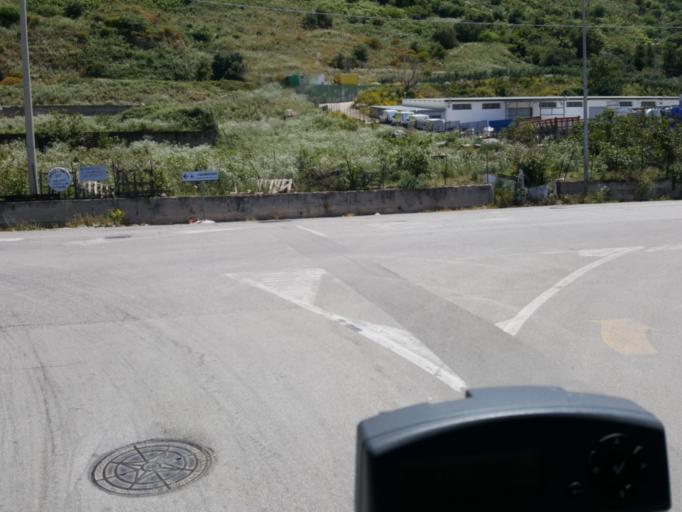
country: IT
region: Sicily
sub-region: Palermo
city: Carini
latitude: 38.1500
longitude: 13.2075
